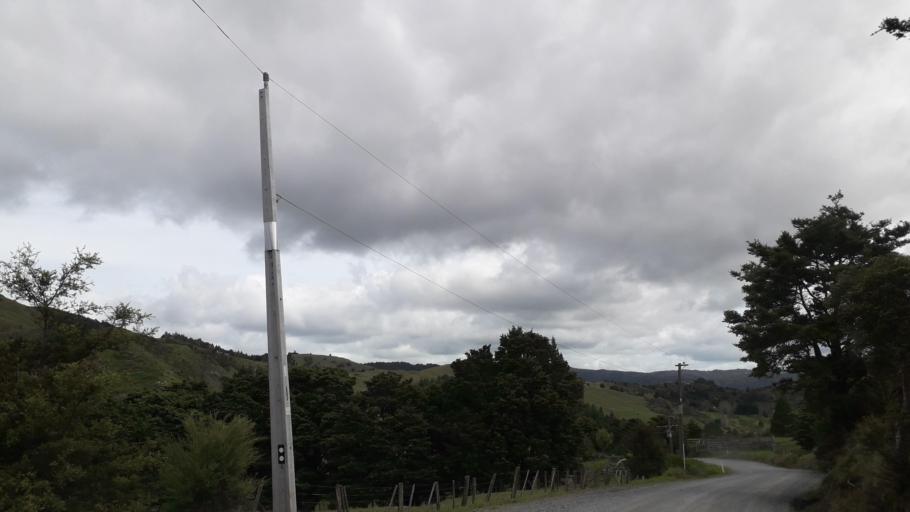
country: NZ
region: Northland
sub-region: Far North District
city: Kerikeri
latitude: -35.1257
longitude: 173.7452
